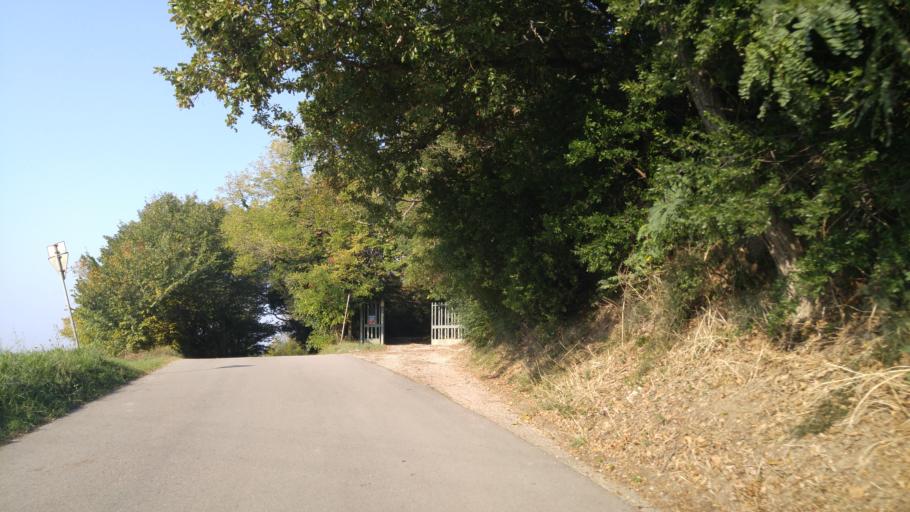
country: IT
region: The Marches
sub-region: Provincia di Pesaro e Urbino
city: Fenile
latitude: 43.8631
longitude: 12.9643
